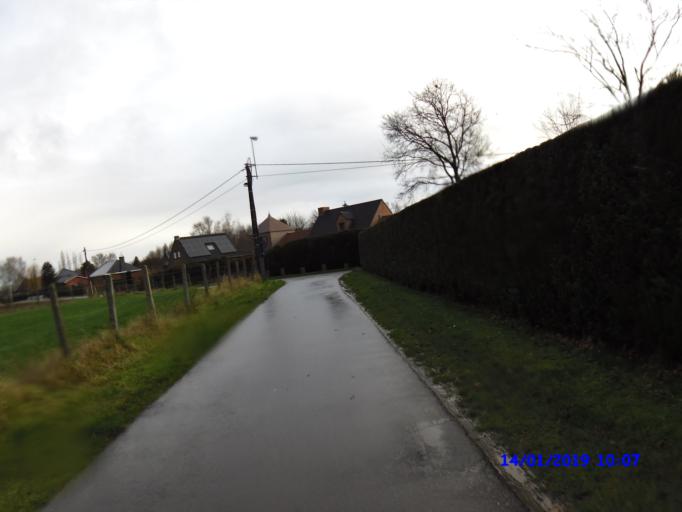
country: BE
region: Flanders
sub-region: Provincie Oost-Vlaanderen
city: Buggenhout
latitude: 51.0022
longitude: 4.1863
